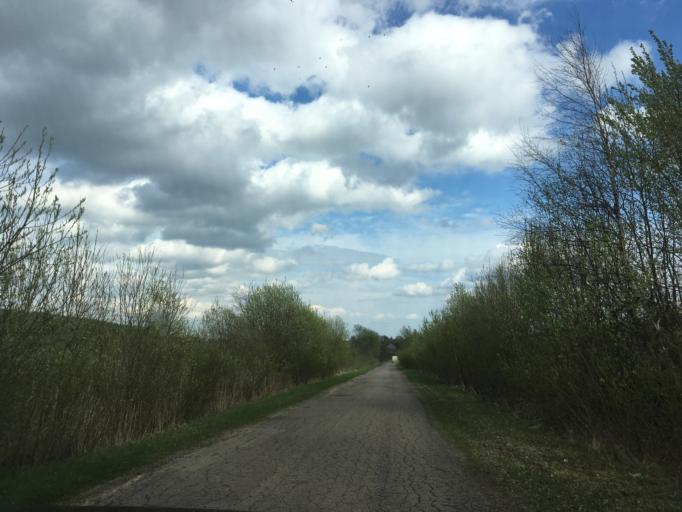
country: PL
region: Podlasie
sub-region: Suwalki
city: Suwalki
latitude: 54.3704
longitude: 22.9081
